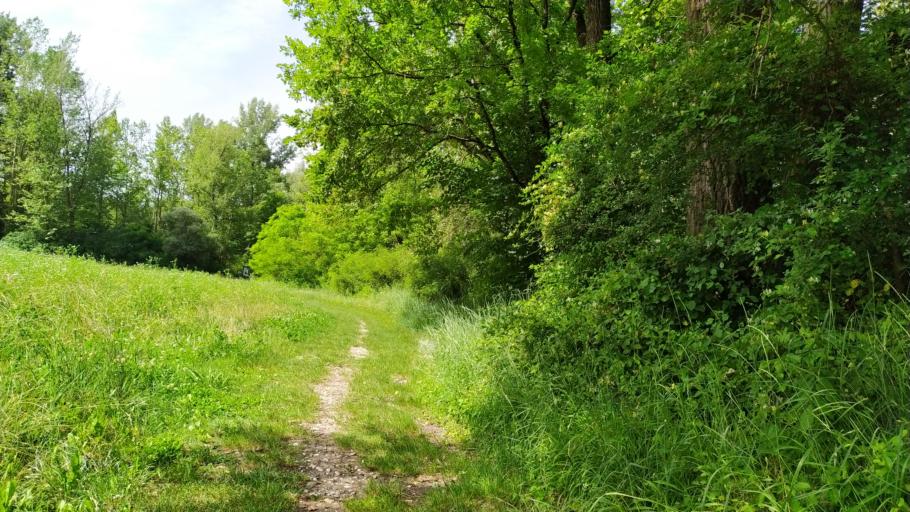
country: IT
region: Veneto
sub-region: Provincia di Treviso
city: Sernaglia della Battaglia
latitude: 45.8553
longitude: 12.1425
